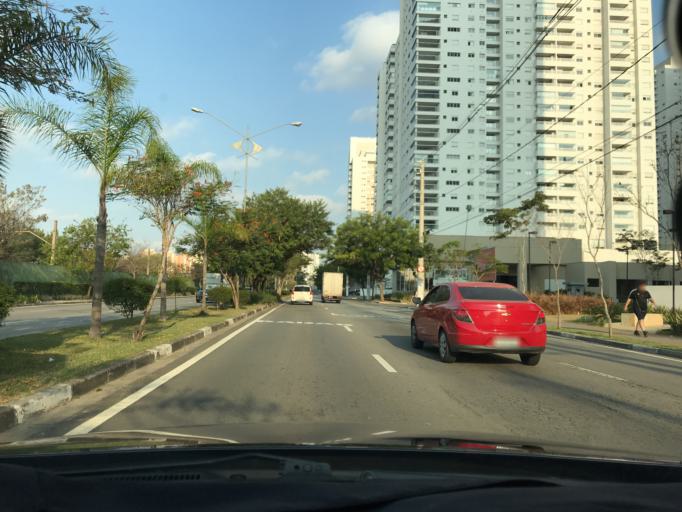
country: BR
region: Sao Paulo
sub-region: Osasco
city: Osasco
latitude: -23.5336
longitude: -46.7709
